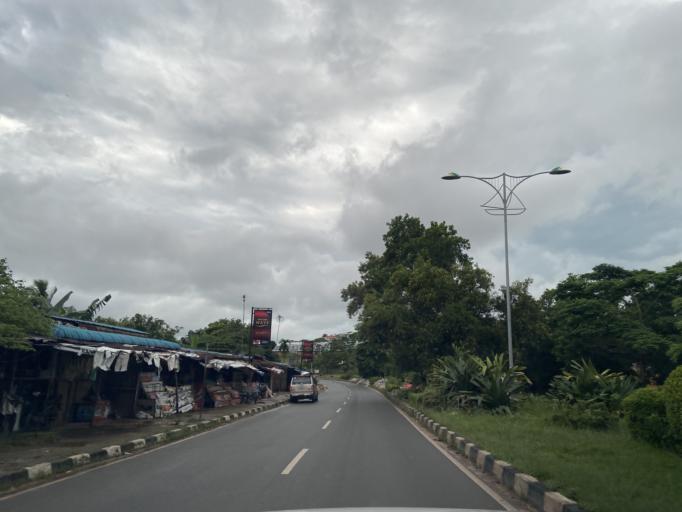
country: SG
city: Singapore
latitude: 1.0373
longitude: 103.9975
